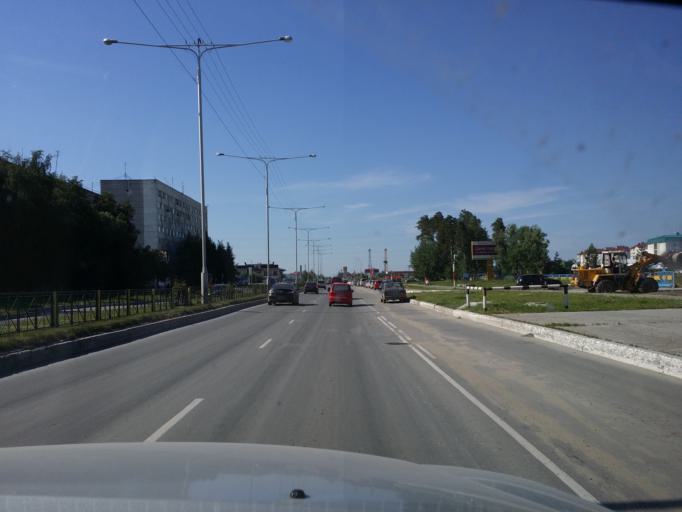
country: RU
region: Khanty-Mansiyskiy Avtonomnyy Okrug
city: Nizhnevartovsk
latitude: 60.9487
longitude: 76.5643
